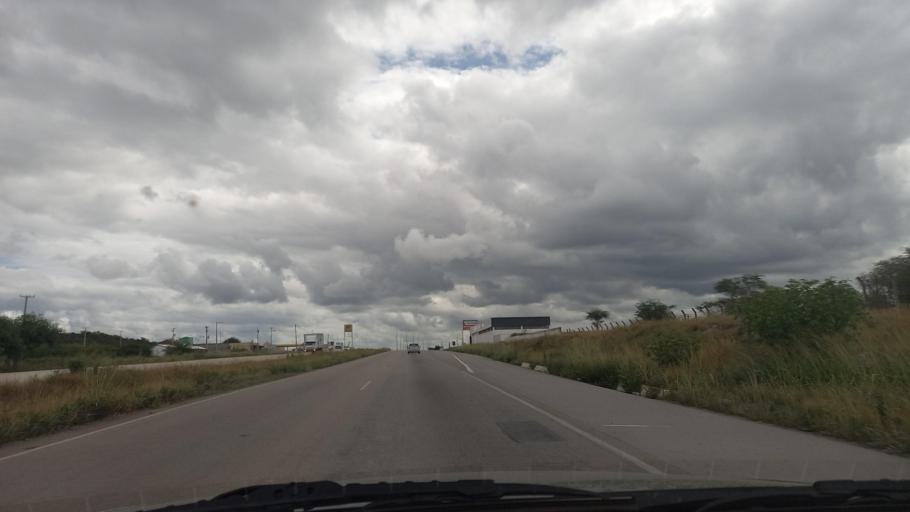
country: BR
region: Pernambuco
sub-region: Caruaru
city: Caruaru
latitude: -8.3204
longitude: -36.0757
